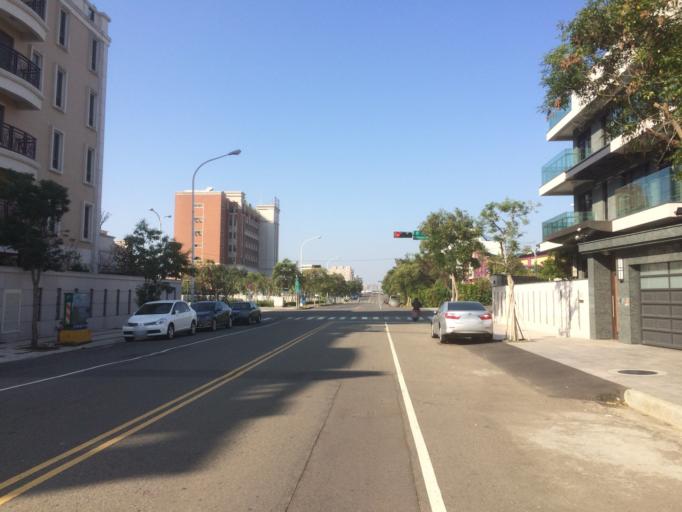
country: TW
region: Taiwan
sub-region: Taichung City
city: Taichung
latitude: 24.1801
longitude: 120.7140
